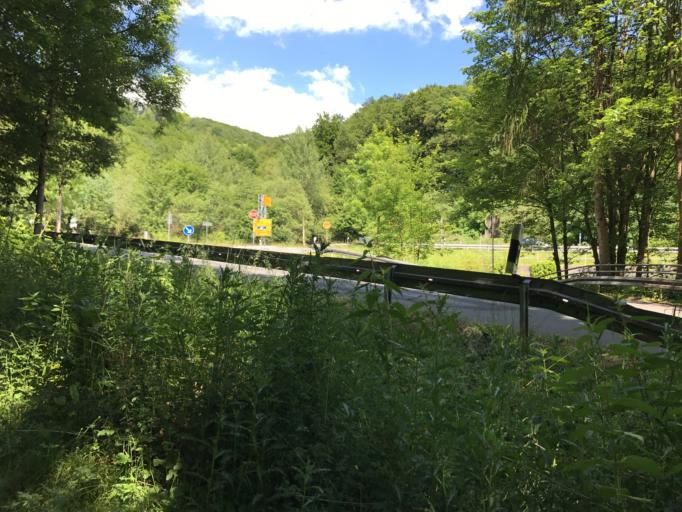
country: DE
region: Hesse
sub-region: Regierungsbezirk Darmstadt
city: Schlangenbad
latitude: 50.1009
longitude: 8.1048
